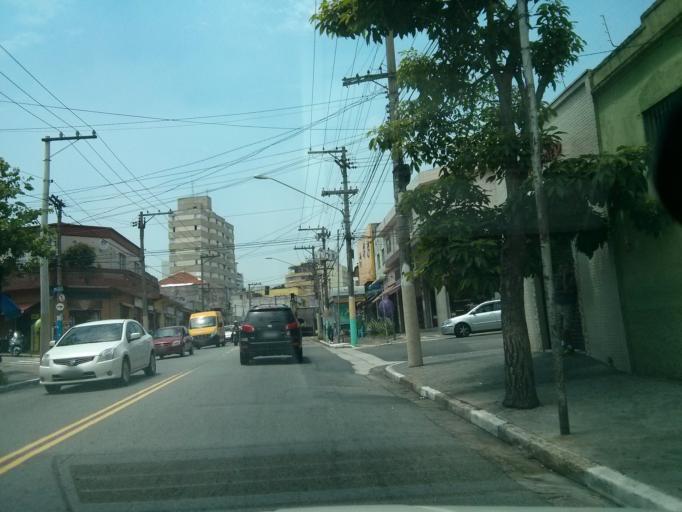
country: BR
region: Sao Paulo
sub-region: Sao Paulo
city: Sao Paulo
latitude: -23.6009
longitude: -46.6154
